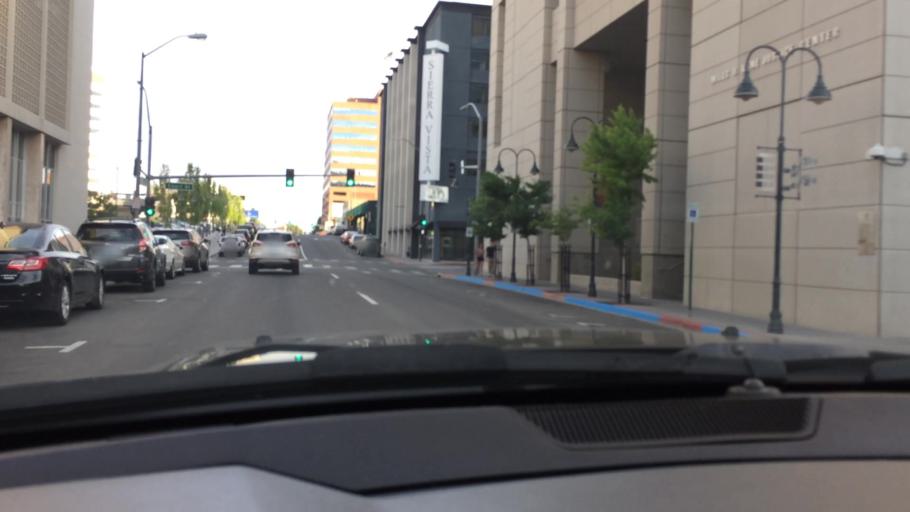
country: US
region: Nevada
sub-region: Washoe County
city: Reno
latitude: 39.5239
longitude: -119.8133
